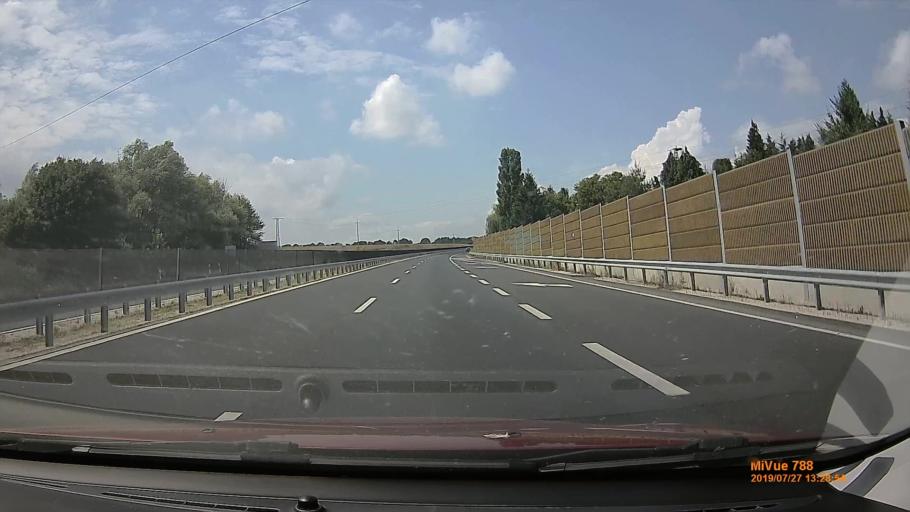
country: HU
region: Veszprem
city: Herend
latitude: 47.1312
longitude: 17.7443
